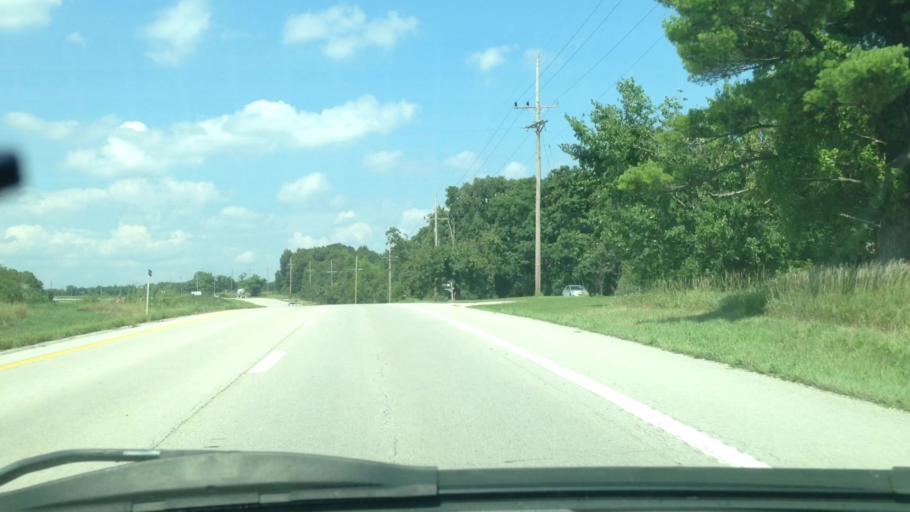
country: US
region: Missouri
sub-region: Lincoln County
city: Troy
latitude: 39.1096
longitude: -90.9603
